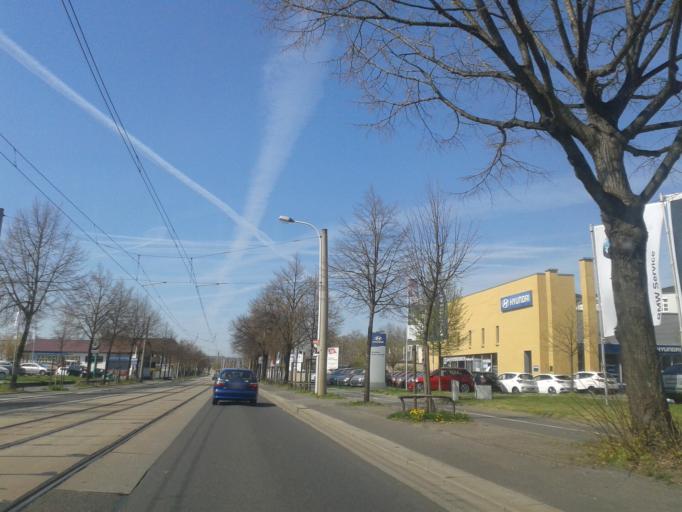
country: DE
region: Saxony
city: Dresden
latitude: 51.0597
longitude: 13.6988
